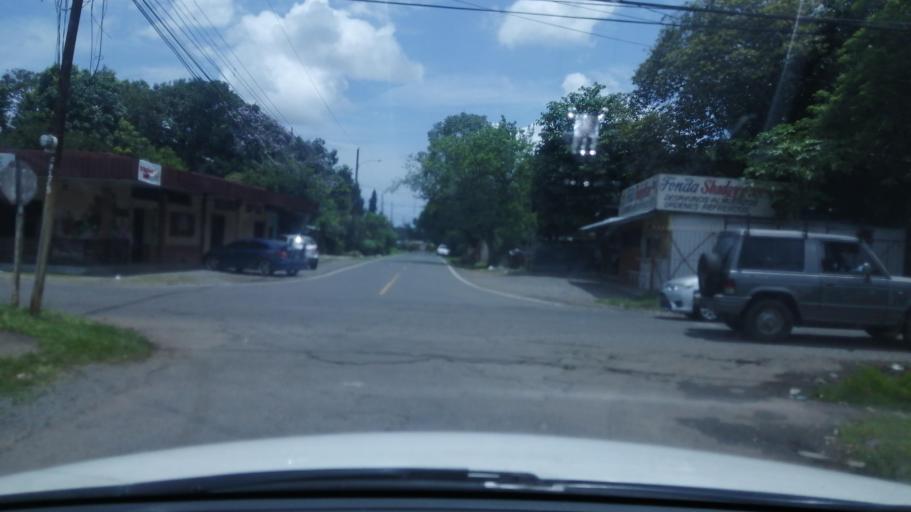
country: PA
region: Chiriqui
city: David
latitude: 8.4226
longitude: -82.4251
